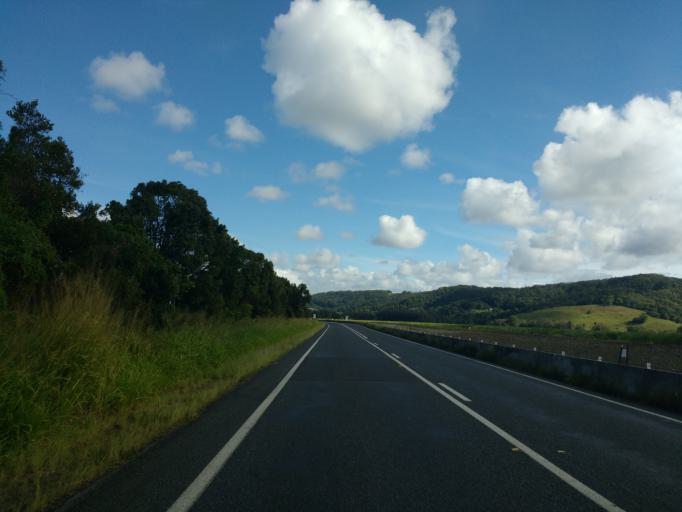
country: AU
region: New South Wales
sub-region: Ballina
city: Ballina
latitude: -28.8820
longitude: 153.4855
